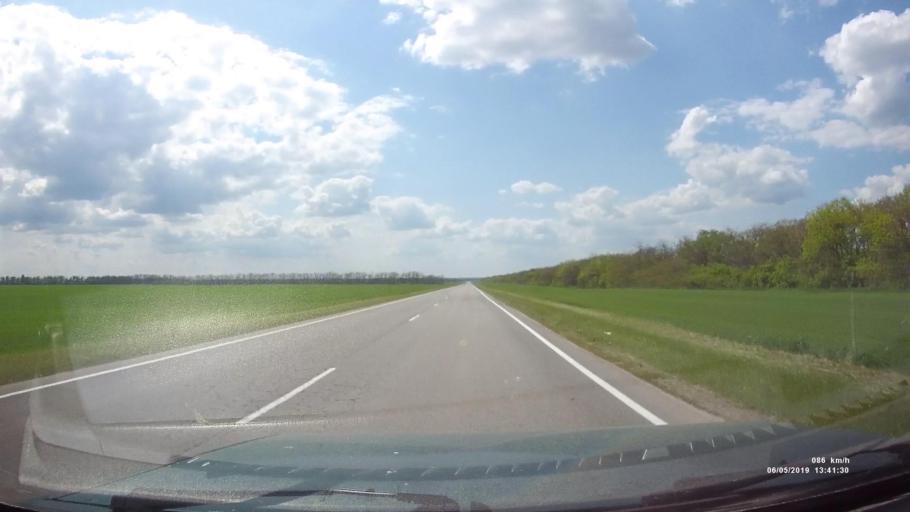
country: RU
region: Rostov
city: Semikarakorsk
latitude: 47.6621
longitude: 40.6754
